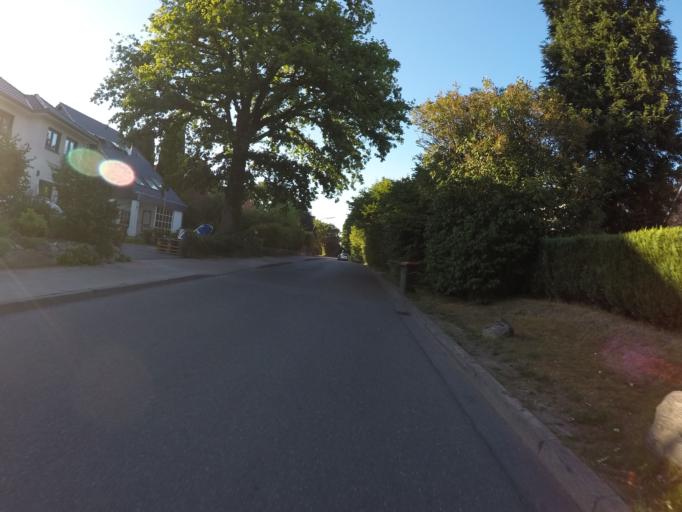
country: DE
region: Hamburg
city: Duvenstedt
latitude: 53.7004
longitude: 10.1115
